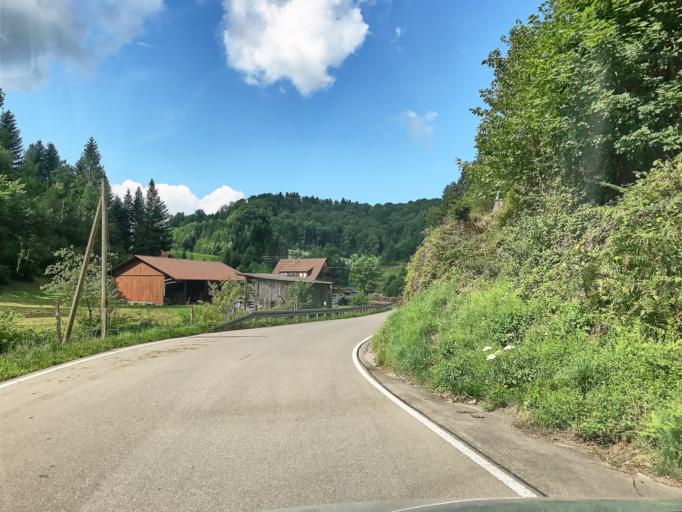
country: DE
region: Baden-Wuerttemberg
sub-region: Freiburg Region
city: Nordrach
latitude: 48.4191
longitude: 8.1087
